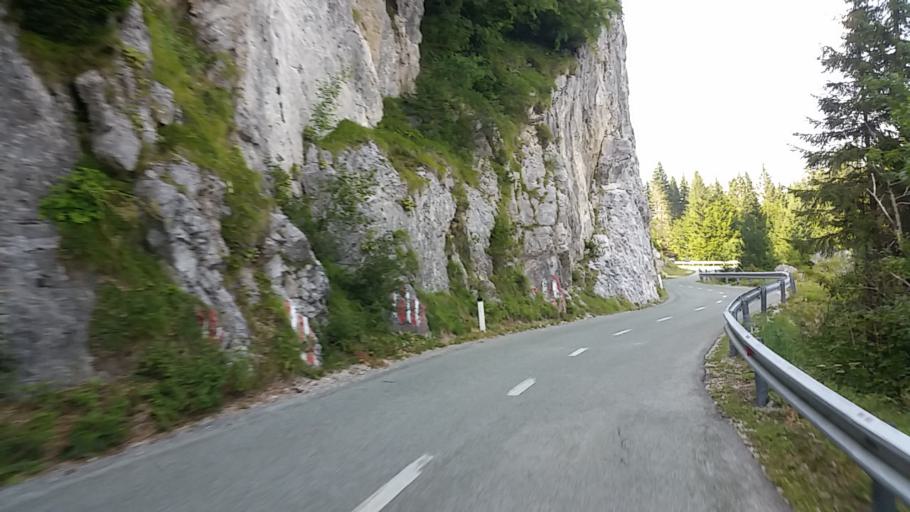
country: SI
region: Bohinj
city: Bohinjska Bistrica
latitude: 46.2356
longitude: 14.0204
